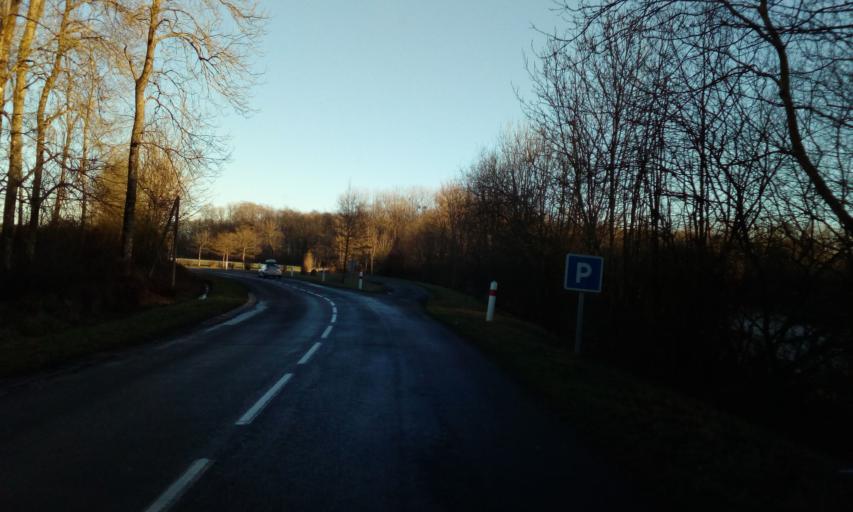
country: FR
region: Champagne-Ardenne
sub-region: Departement des Ardennes
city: Signy-le-Petit
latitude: 49.7408
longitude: 4.2989
